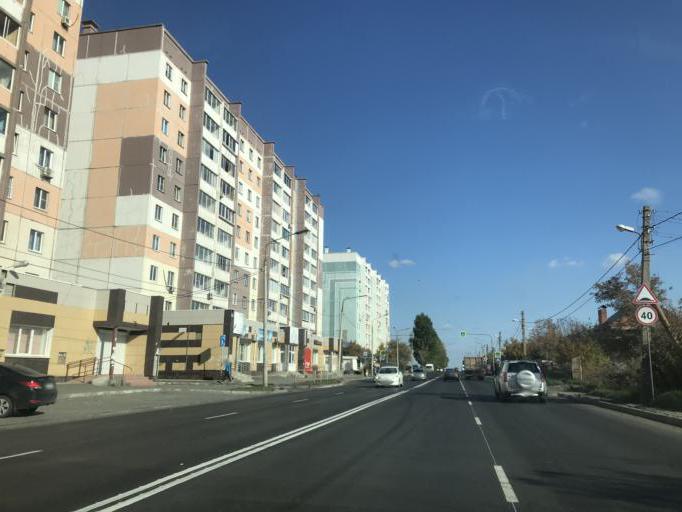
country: RU
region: Chelyabinsk
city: Roshchino
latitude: 55.2346
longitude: 61.3045
